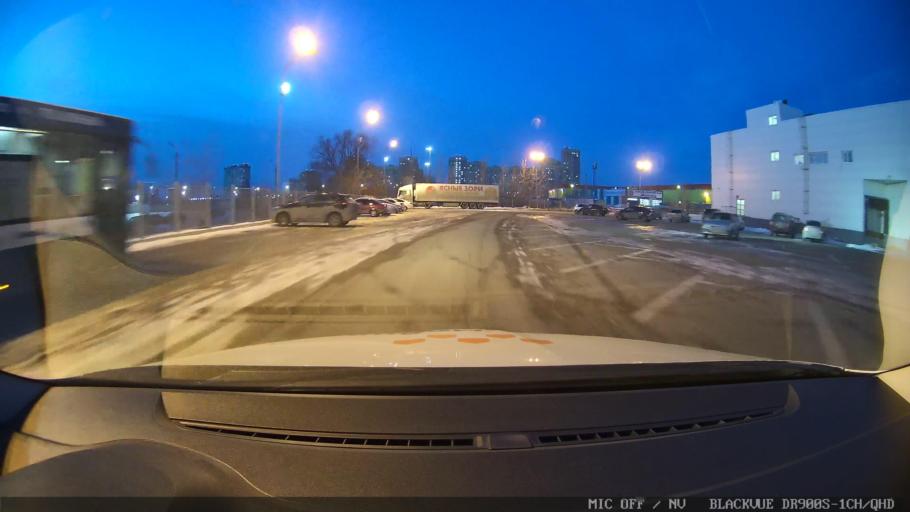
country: RU
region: Tatarstan
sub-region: Gorod Kazan'
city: Kazan
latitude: 55.7702
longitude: 49.2155
